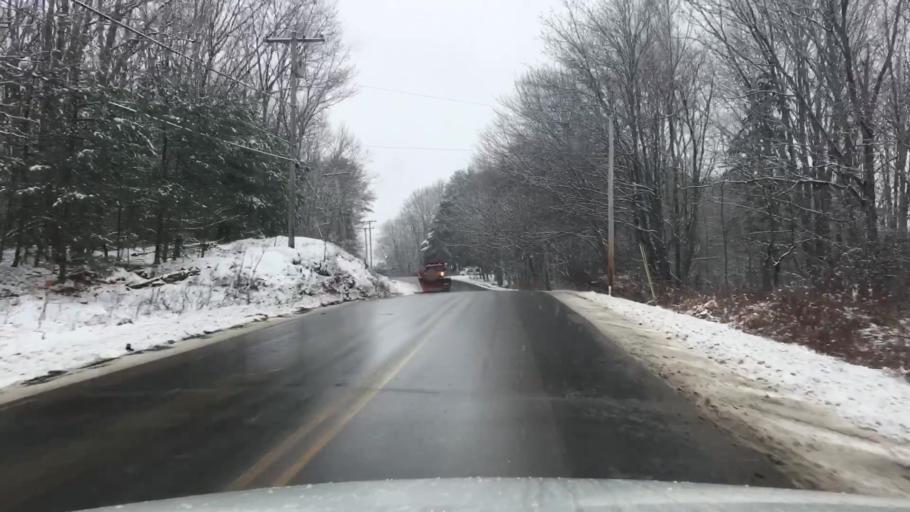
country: US
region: Maine
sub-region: Knox County
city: Warren
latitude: 44.1367
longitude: -69.2666
